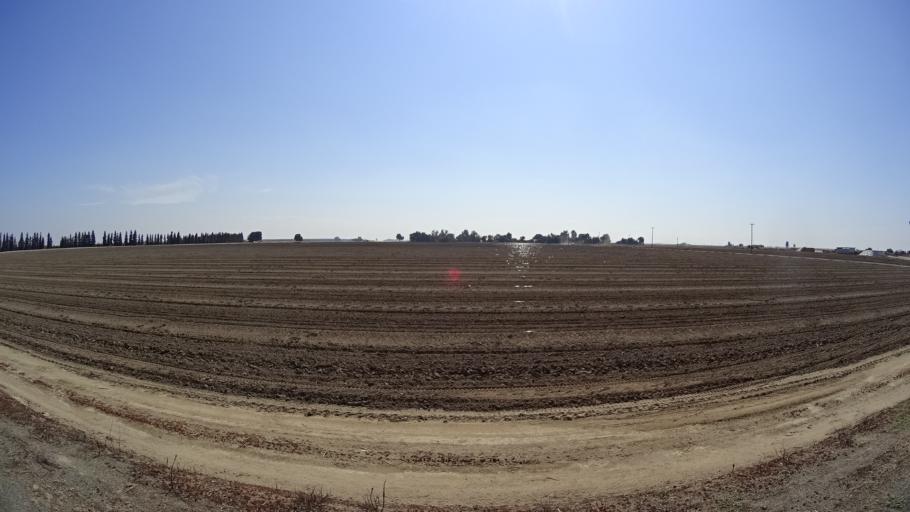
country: US
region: California
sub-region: Kings County
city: Lucerne
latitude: 36.4096
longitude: -119.5830
